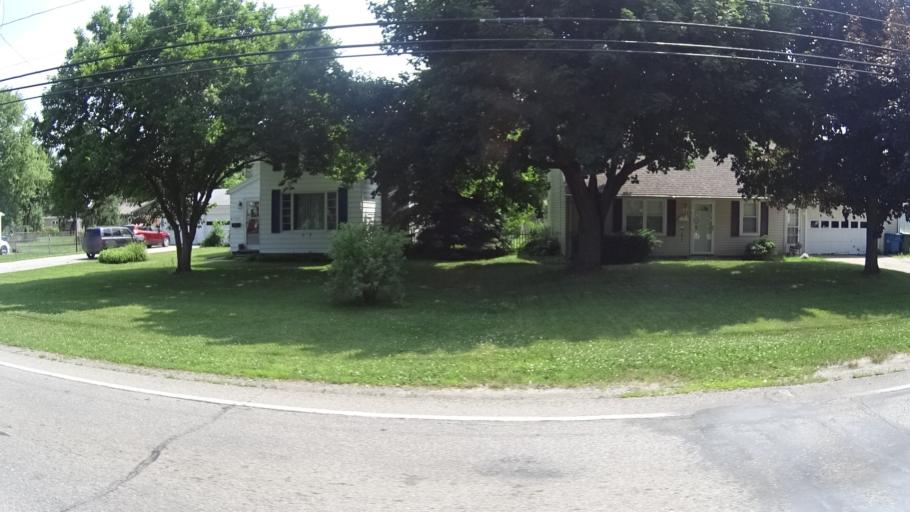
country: US
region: Ohio
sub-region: Lorain County
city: Vermilion
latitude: 41.4148
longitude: -82.3656
